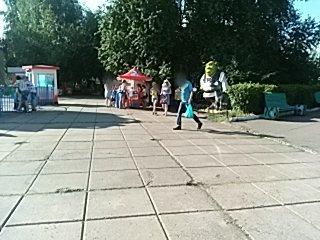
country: RU
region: Tatarstan
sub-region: Tukayevskiy Rayon
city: Naberezhnyye Chelny
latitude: 55.7547
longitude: 52.4259
